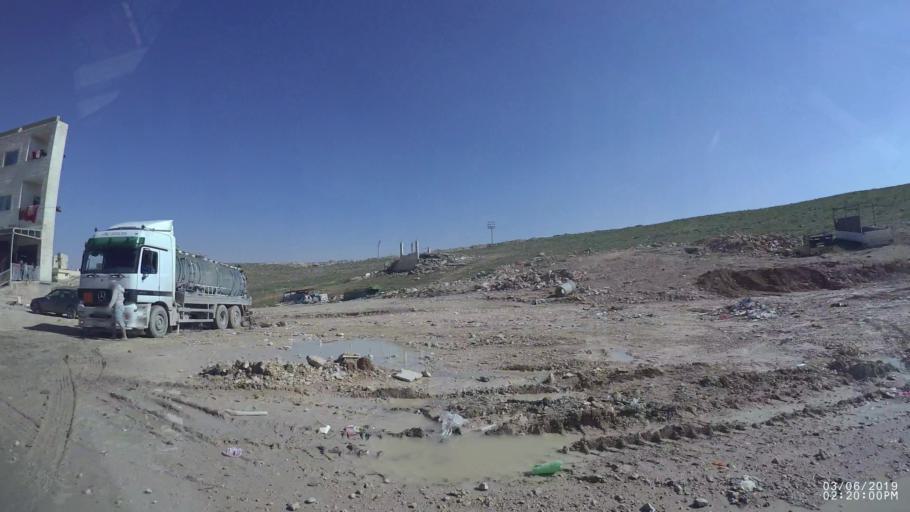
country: JO
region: Zarqa
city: Russeifa
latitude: 32.0378
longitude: 36.0497
